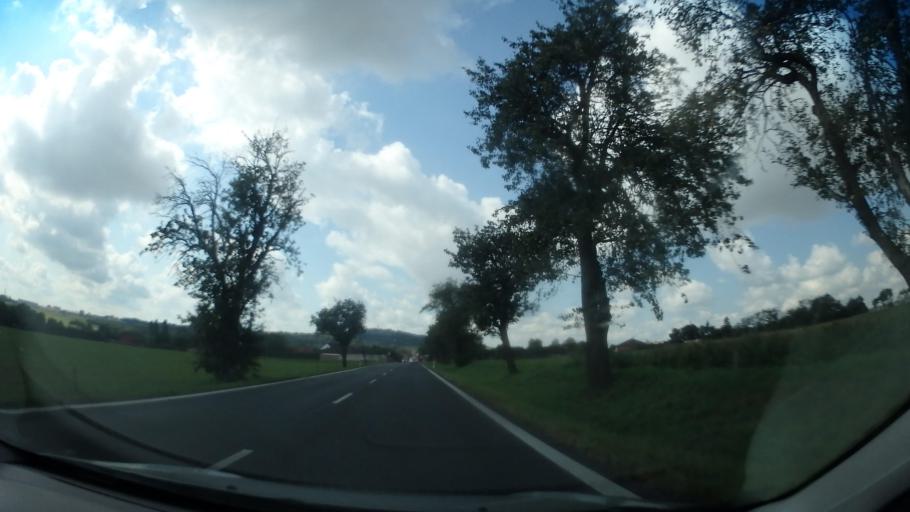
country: CZ
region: Central Bohemia
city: Cervene Pecky
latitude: 49.9476
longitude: 15.2143
